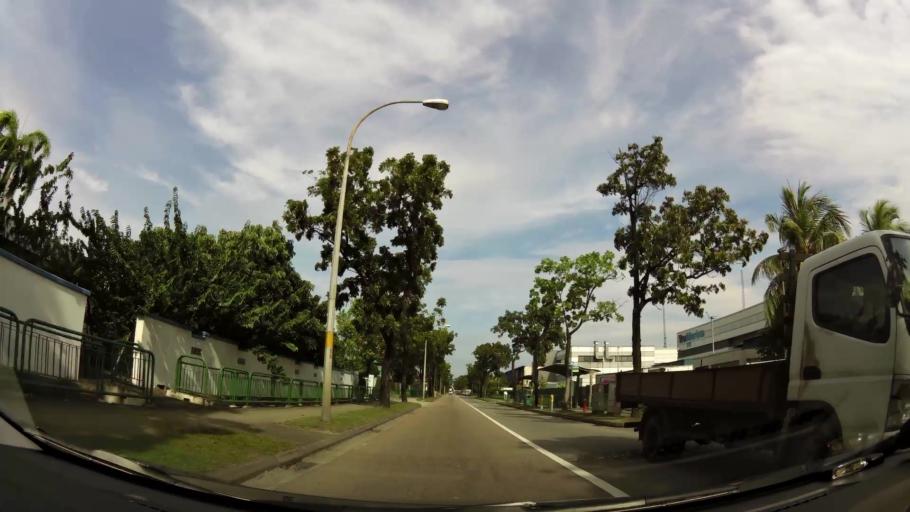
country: MY
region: Johor
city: Johor Bahru
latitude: 1.3145
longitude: 103.6544
